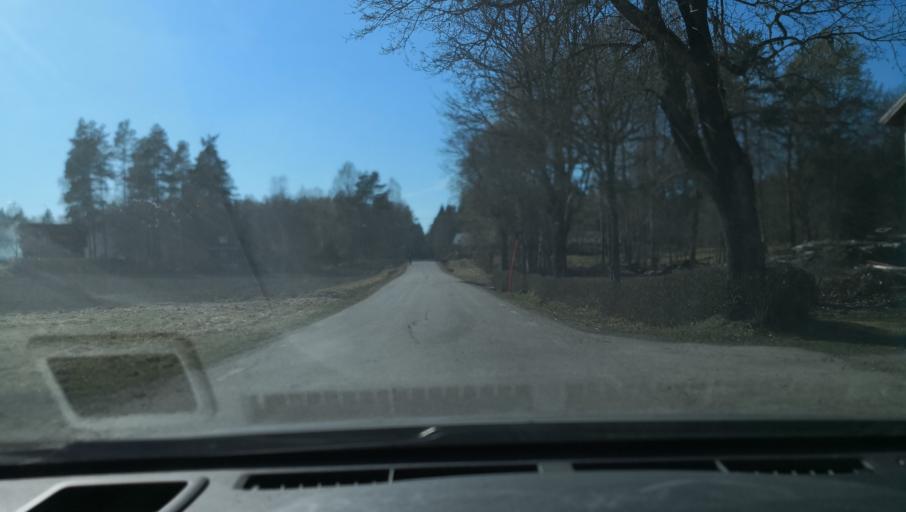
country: SE
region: Dalarna
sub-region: Avesta Kommun
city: Horndal
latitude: 60.0823
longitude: 16.4486
